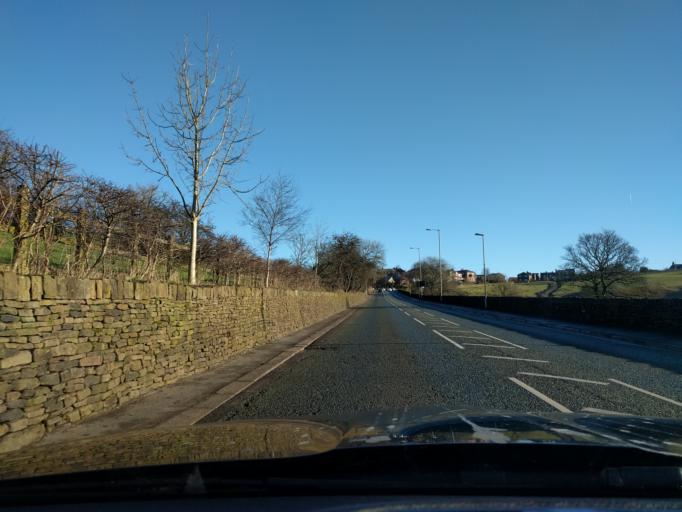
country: GB
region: England
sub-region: Borough of Tameside
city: Mossley
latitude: 53.5374
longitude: -2.0480
